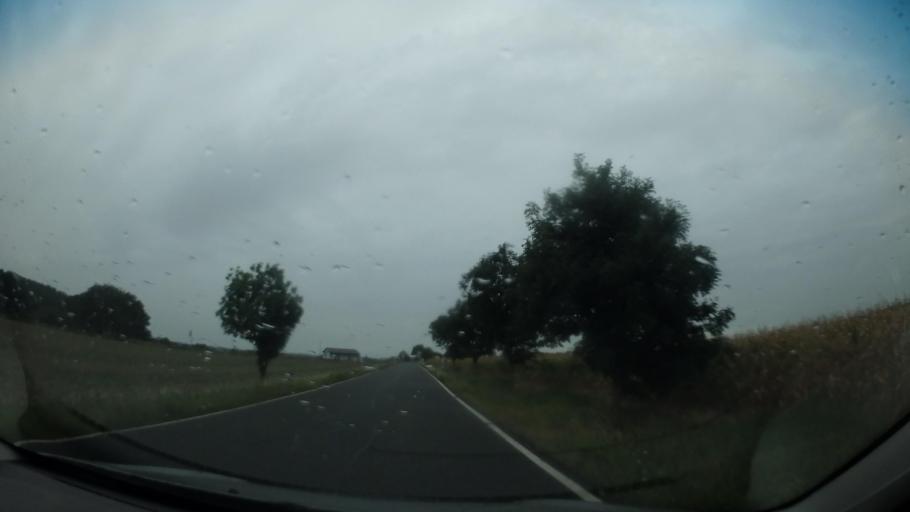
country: CZ
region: Central Bohemia
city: Loucen
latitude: 50.2381
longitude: 14.9972
